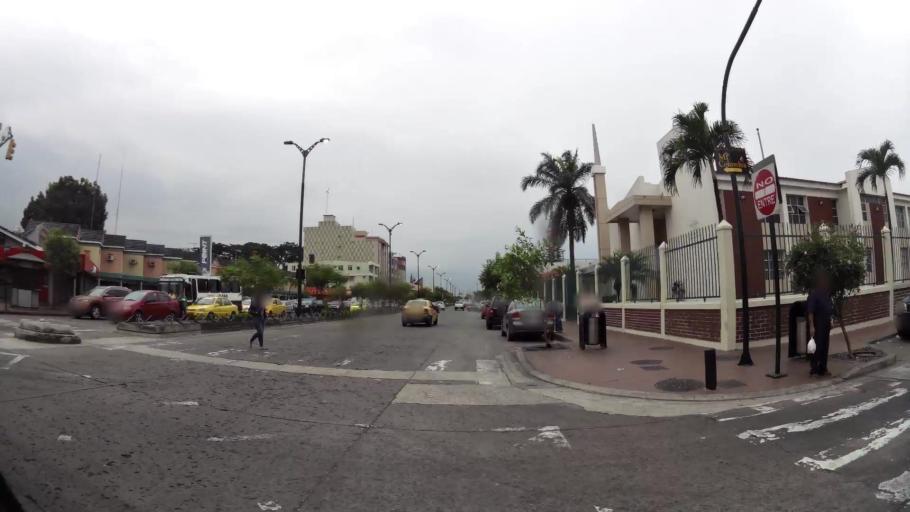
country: EC
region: Guayas
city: Eloy Alfaro
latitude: -2.1374
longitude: -79.9000
